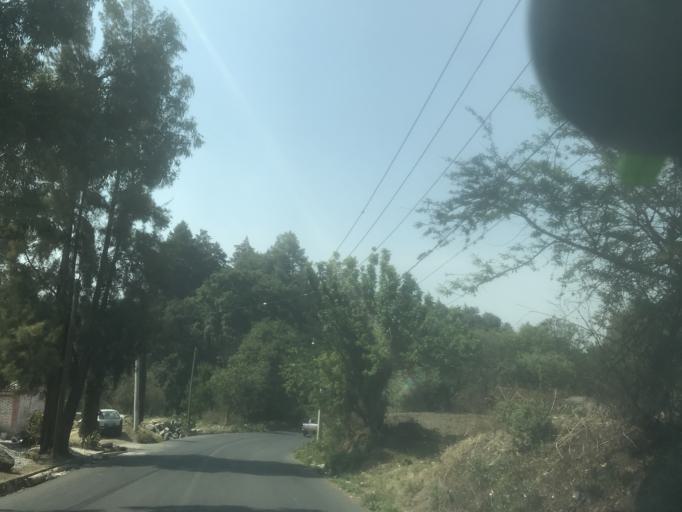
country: MX
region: Mexico
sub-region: Atlautla
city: San Juan Tepecoculco
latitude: 18.9939
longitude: -98.7942
